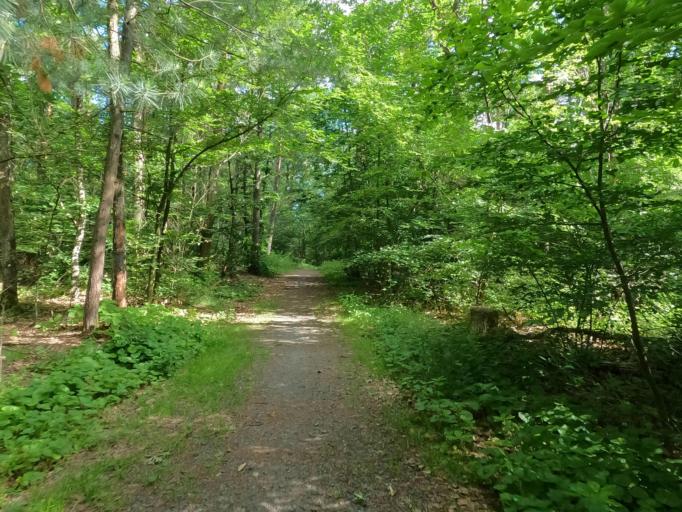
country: DE
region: Hesse
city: Niederrad
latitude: 50.0551
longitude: 8.6524
